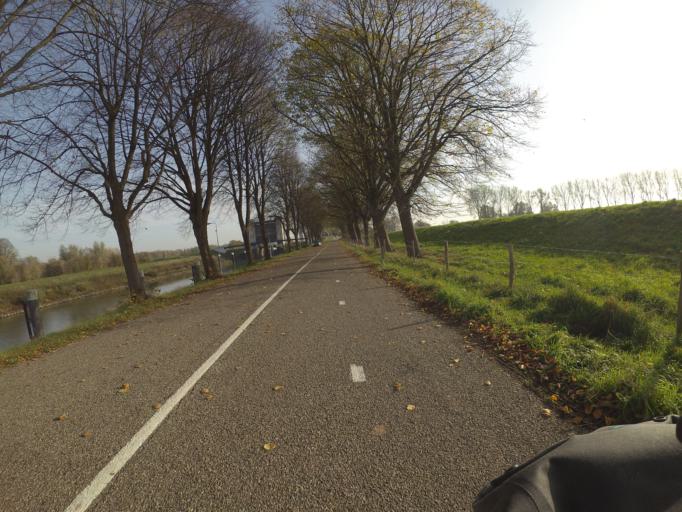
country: NL
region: Gelderland
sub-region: Gemeente Maasdriel
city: Heerewaarden
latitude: 51.7996
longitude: 5.3545
